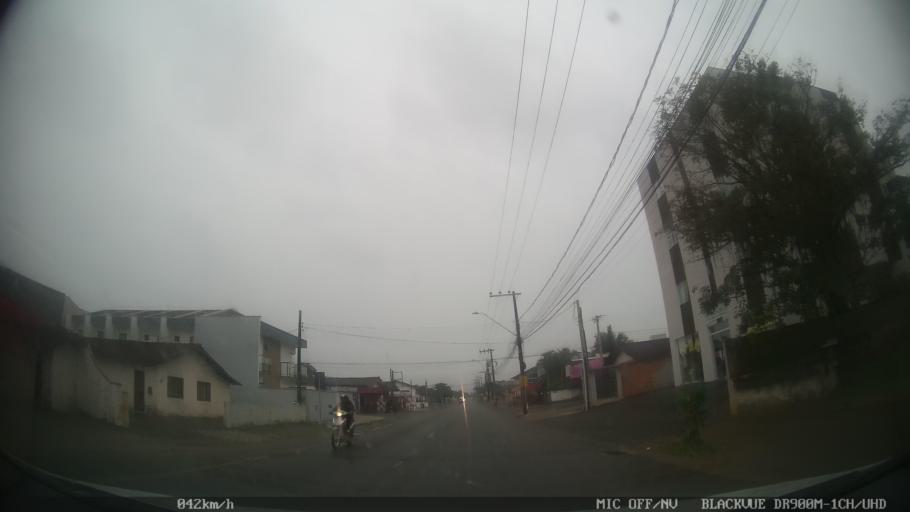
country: BR
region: Santa Catarina
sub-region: Joinville
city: Joinville
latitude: -26.2738
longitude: -48.8034
